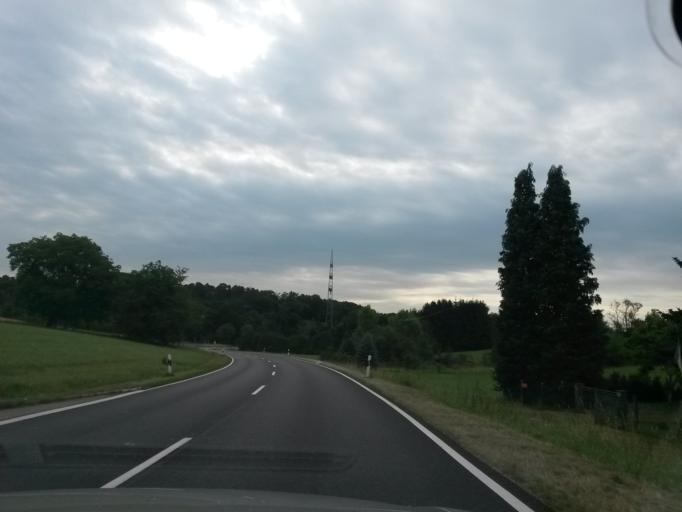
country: DE
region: Baden-Wuerttemberg
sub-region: Karlsruhe Region
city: Birkenfeld
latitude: 48.8972
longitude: 8.6413
